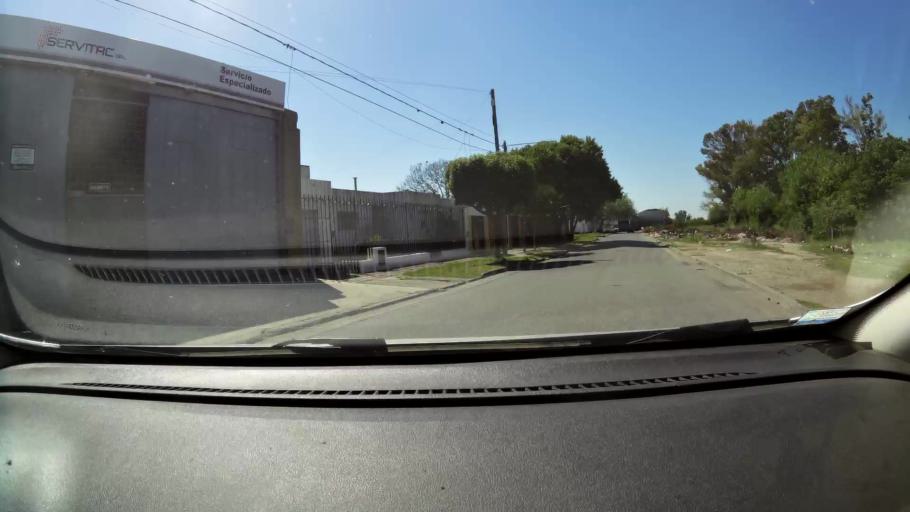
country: AR
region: Cordoba
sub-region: Departamento de Capital
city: Cordoba
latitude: -31.4350
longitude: -64.1343
